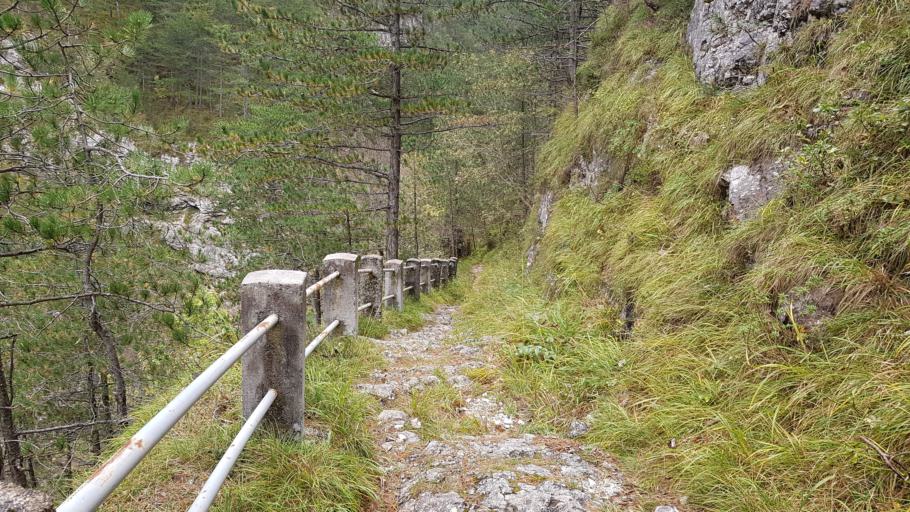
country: IT
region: Friuli Venezia Giulia
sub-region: Provincia di Udine
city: Chiusaforte
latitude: 46.4179
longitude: 13.3235
